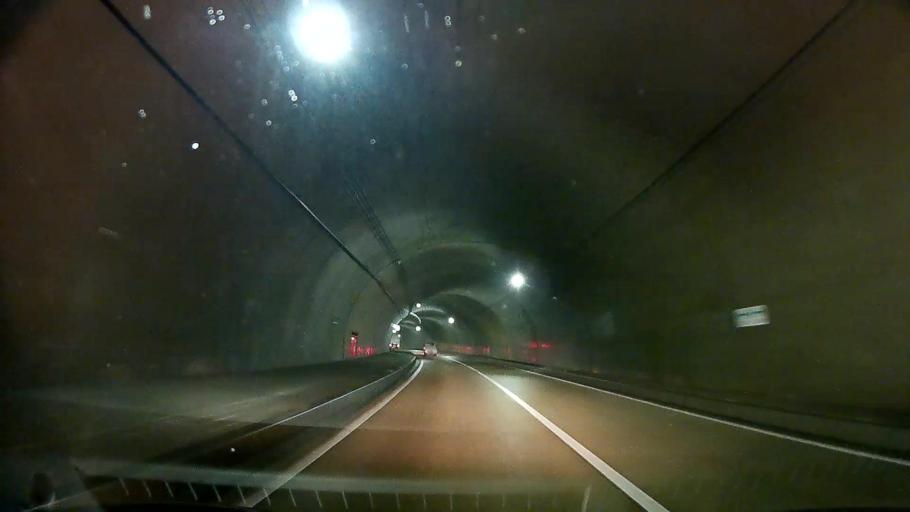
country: JP
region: Gunma
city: Nakanojomachi
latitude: 36.5404
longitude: 138.6967
